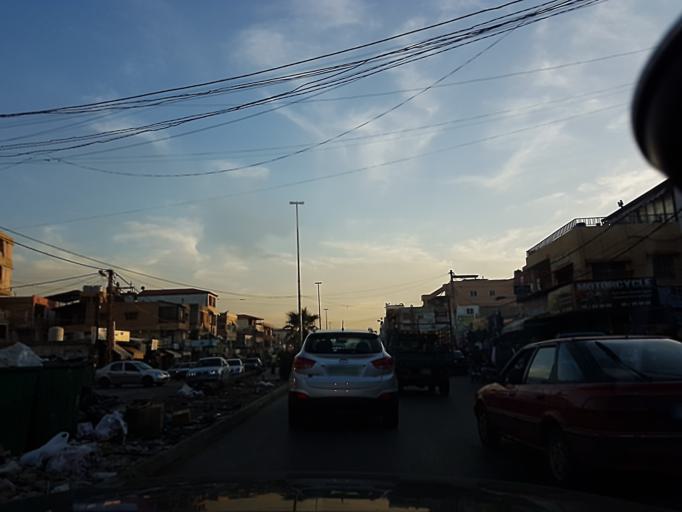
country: LB
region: Beyrouth
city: Beirut
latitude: 33.8462
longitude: 35.4850
